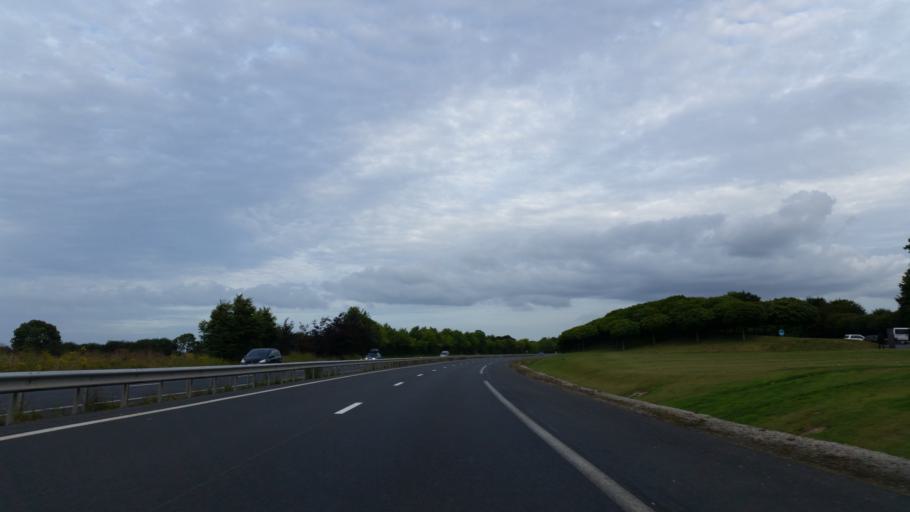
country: FR
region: Lower Normandy
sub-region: Departement du Calvados
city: Grandcamp-Maisy
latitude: 49.3436
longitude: -1.0278
